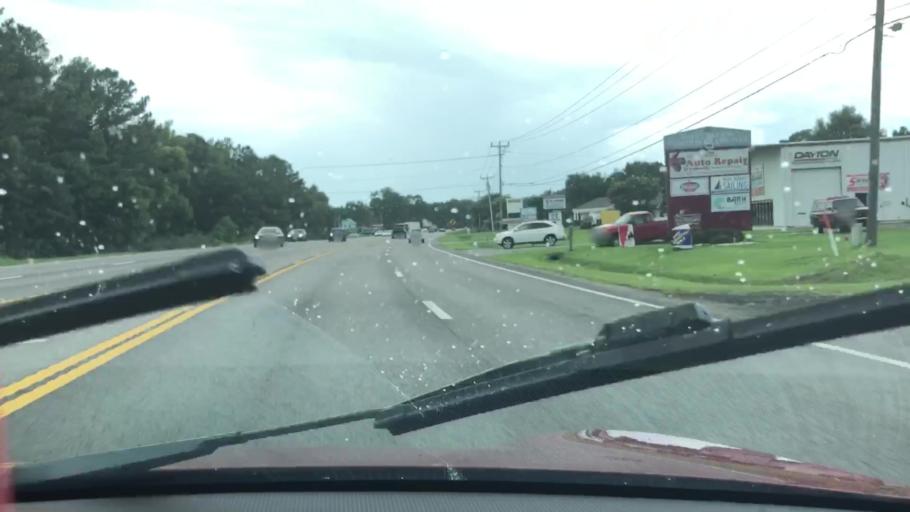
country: US
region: North Carolina
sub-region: Dare County
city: Southern Shores
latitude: 36.0927
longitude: -75.8087
